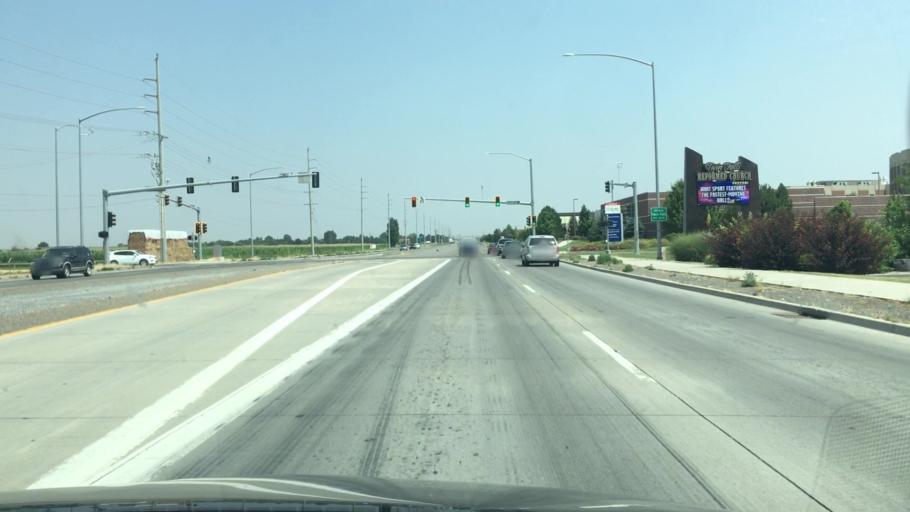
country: US
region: Idaho
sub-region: Twin Falls County
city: Twin Falls
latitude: 42.5916
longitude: -114.5004
